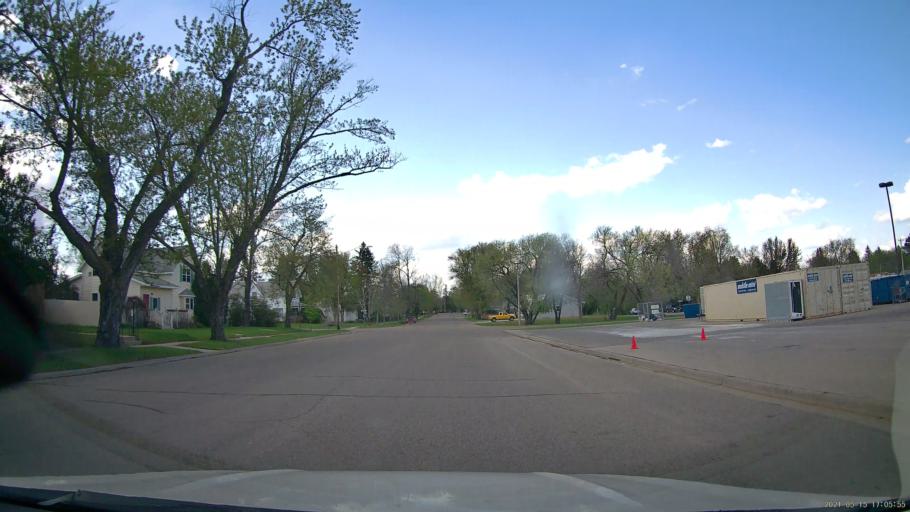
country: US
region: Minnesota
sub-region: Hubbard County
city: Park Rapids
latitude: 46.9229
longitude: -95.0621
